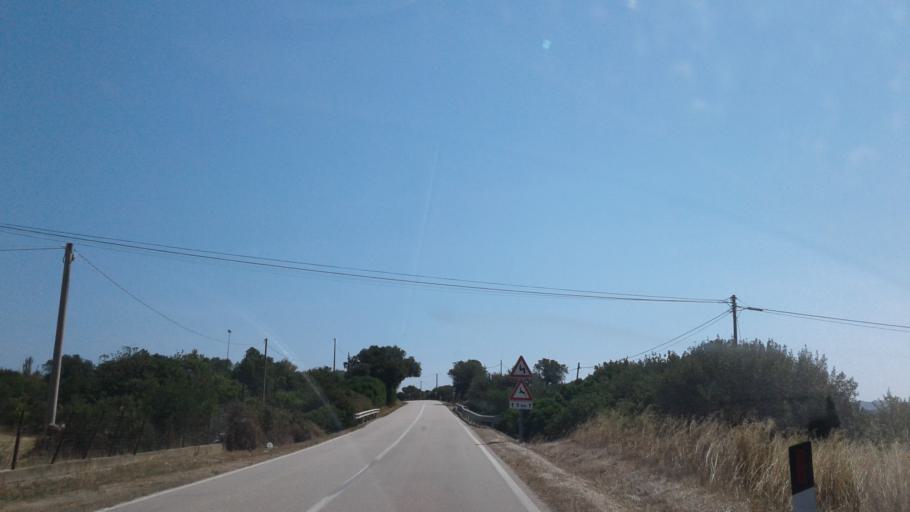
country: IT
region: Sardinia
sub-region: Provincia di Olbia-Tempio
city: Luogosanto
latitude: 41.1157
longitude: 9.2630
